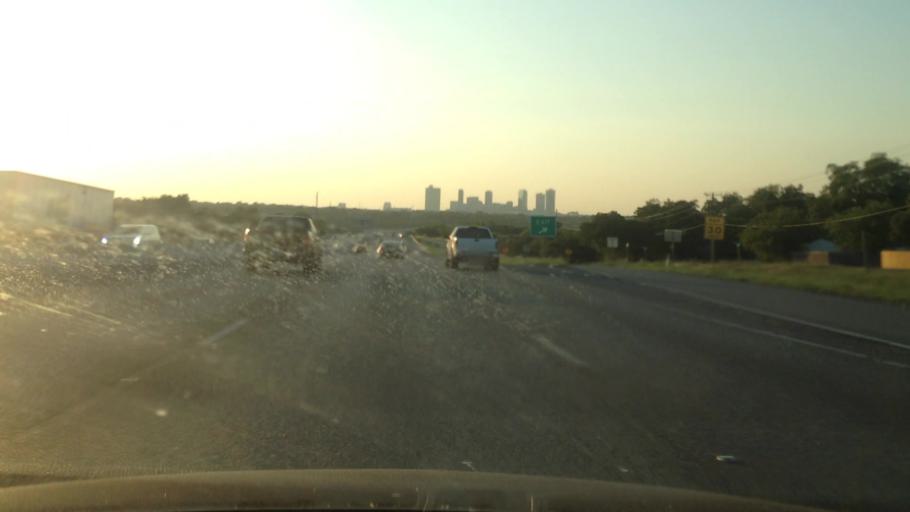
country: US
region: Texas
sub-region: Tarrant County
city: Fort Worth
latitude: 32.7176
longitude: -97.2857
